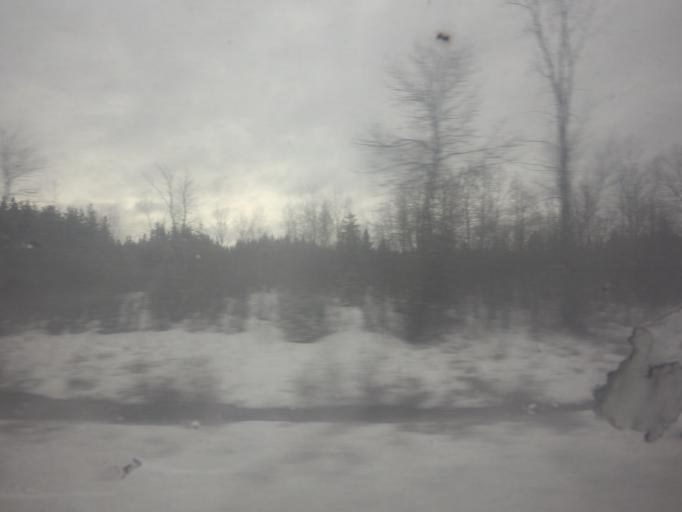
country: CA
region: Ontario
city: Bells Corners
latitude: 45.1147
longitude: -75.8733
